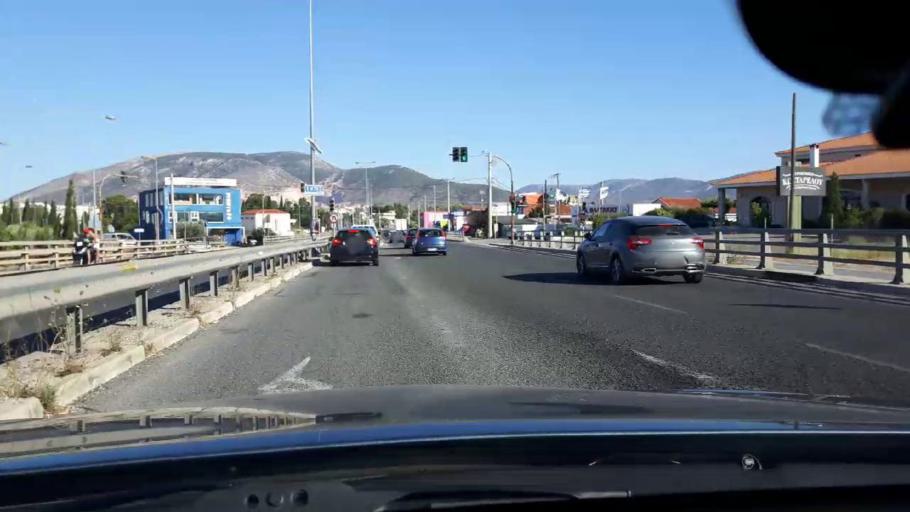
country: GR
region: Attica
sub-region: Nomarchia Anatolikis Attikis
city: Markopoulo
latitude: 37.8885
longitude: 23.9238
